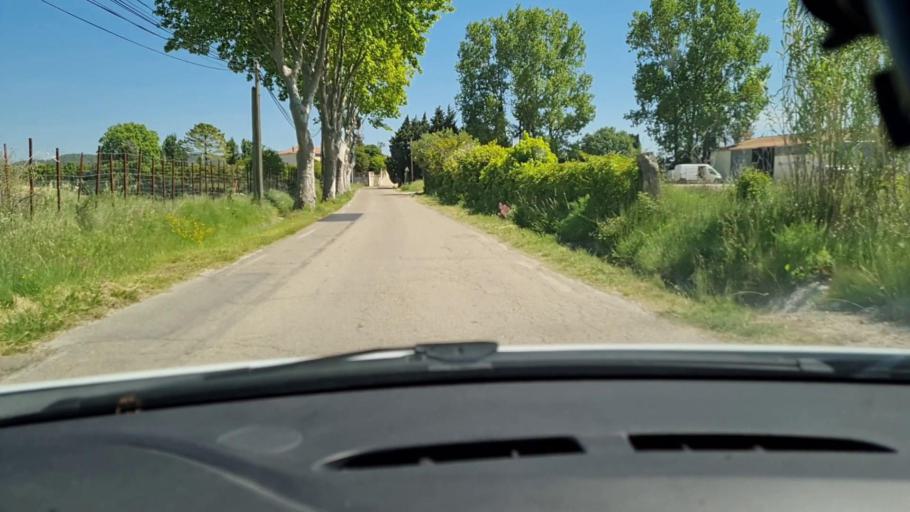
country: FR
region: Languedoc-Roussillon
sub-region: Departement du Gard
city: Clarensac
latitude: 43.8237
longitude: 4.2031
